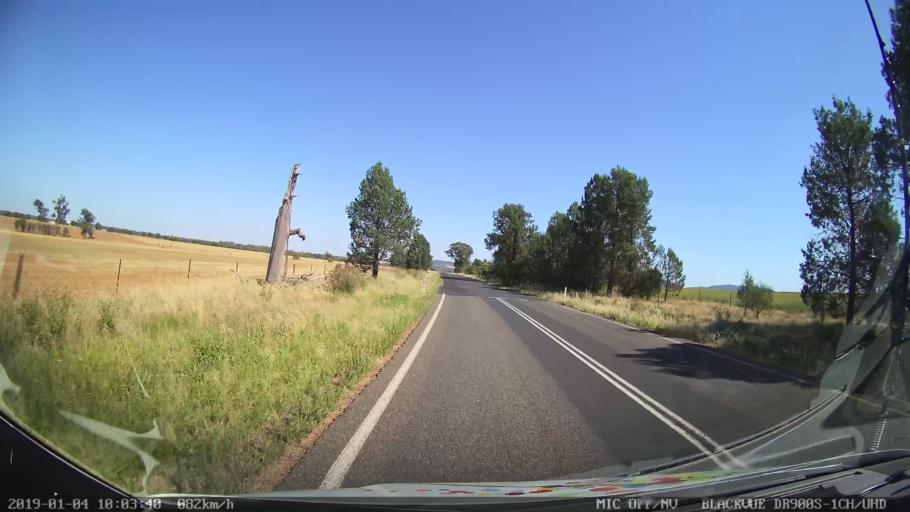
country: AU
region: New South Wales
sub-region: Cabonne
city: Canowindra
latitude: -33.4609
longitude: 148.3636
